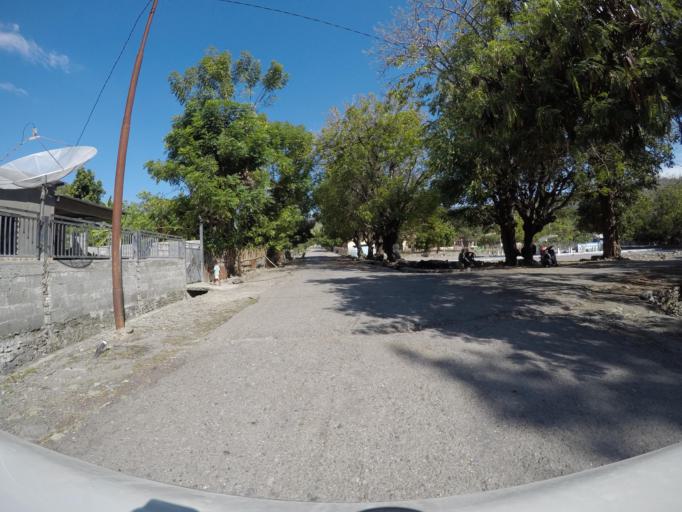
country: TL
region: Liquica
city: Maubara
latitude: -8.6107
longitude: 125.2051
